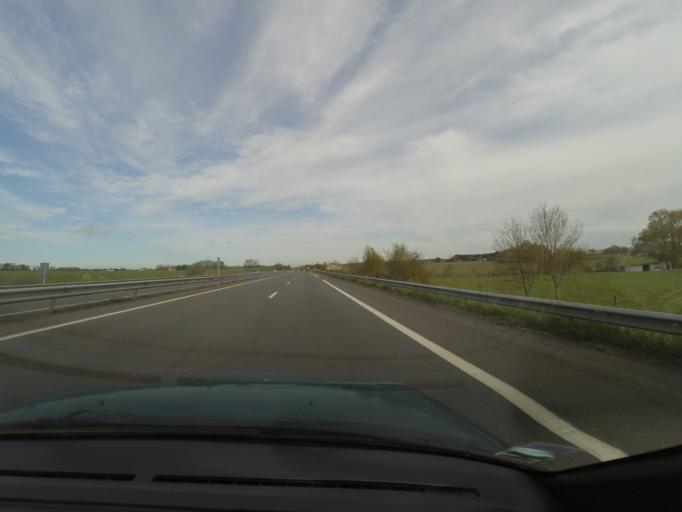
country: FR
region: Pays de la Loire
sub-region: Departement de la Loire-Atlantique
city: Le Bignon
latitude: 47.0944
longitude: -1.4648
